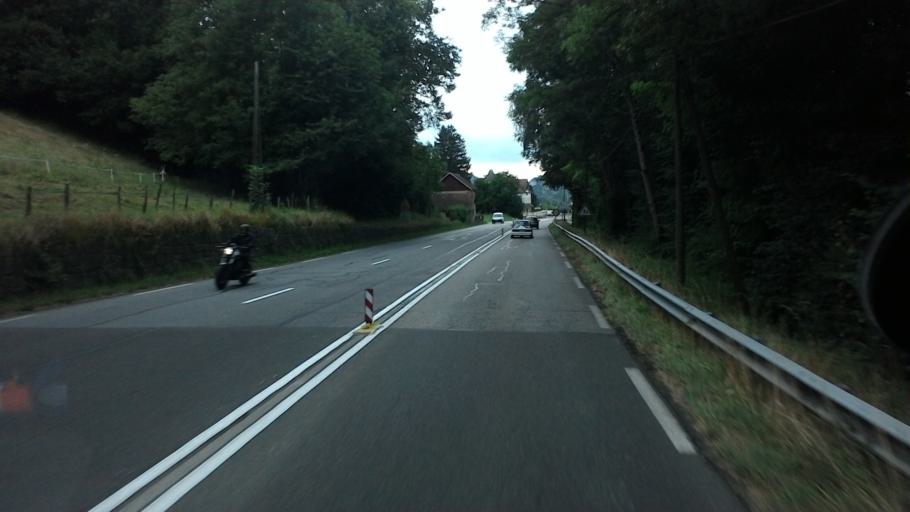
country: FR
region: Rhone-Alpes
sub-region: Departement de la Savoie
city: Yenne
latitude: 45.7029
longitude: 5.7765
